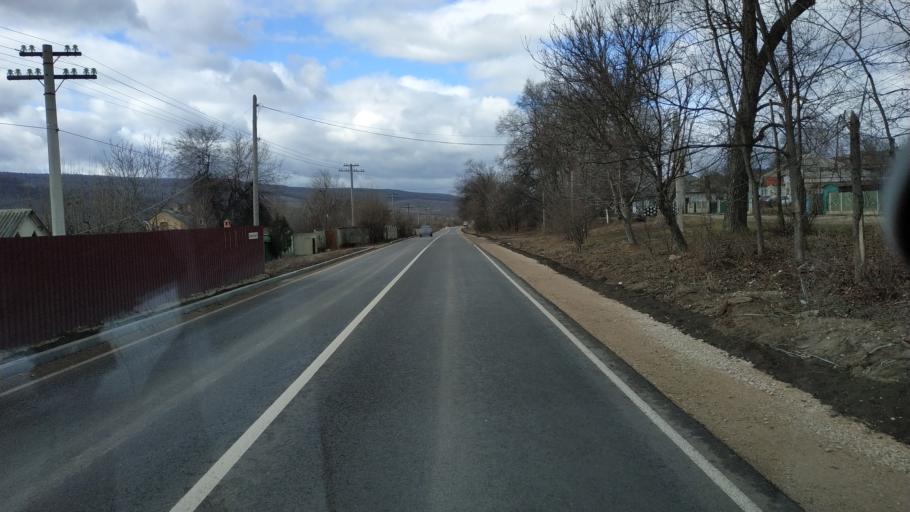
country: MD
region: Stinga Nistrului
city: Bucovat
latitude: 47.1895
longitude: 28.4493
